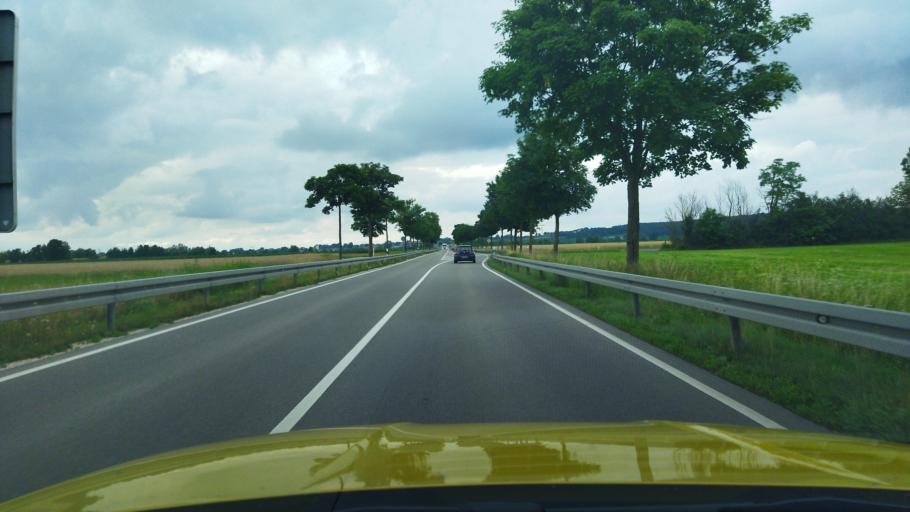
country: DE
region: Bavaria
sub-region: Regierungsbezirk Mittelfranken
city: Gunzenhausen
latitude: 49.1360
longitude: 10.7406
